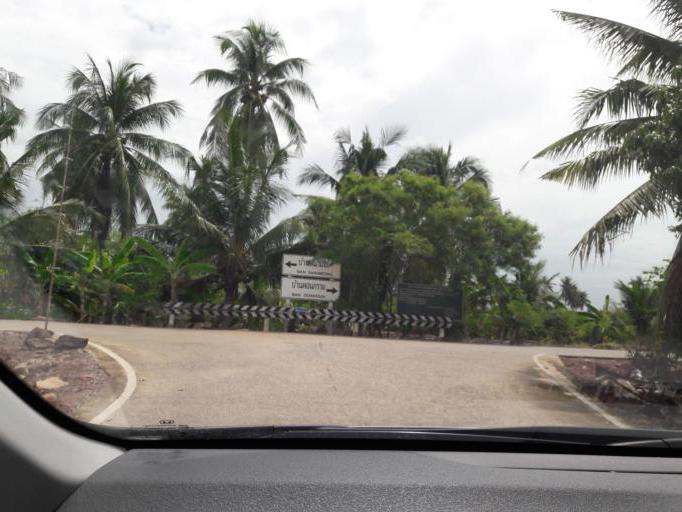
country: TH
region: Ratchaburi
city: Damnoen Saduak
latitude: 13.5475
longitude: 99.9867
